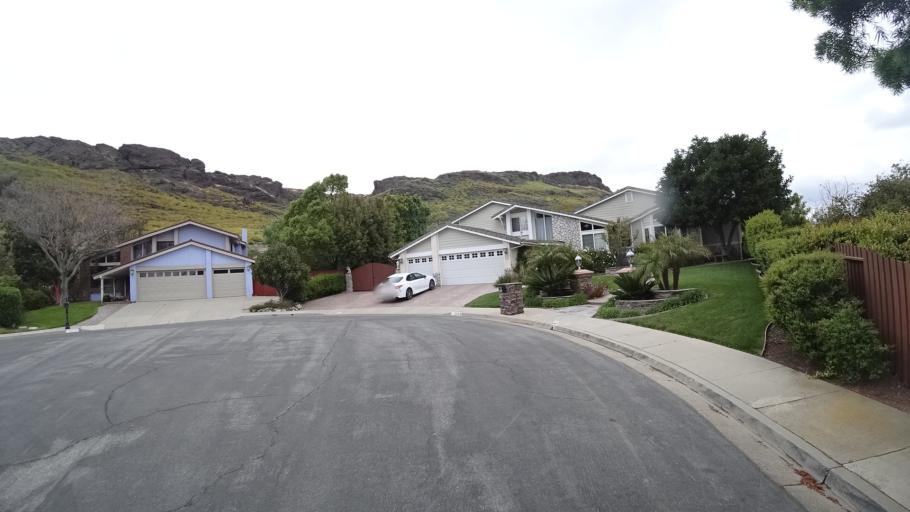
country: US
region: California
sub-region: Ventura County
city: Moorpark
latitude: 34.2240
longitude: -118.8917
